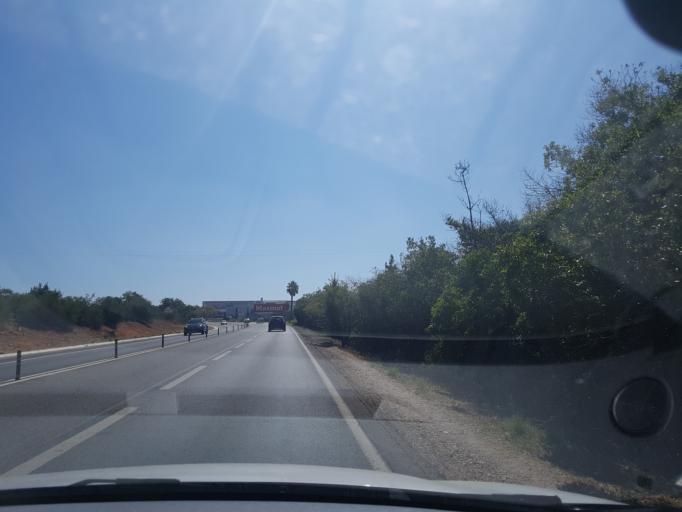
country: PT
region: Faro
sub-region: Albufeira
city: Guia
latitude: 37.1277
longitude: -8.2914
